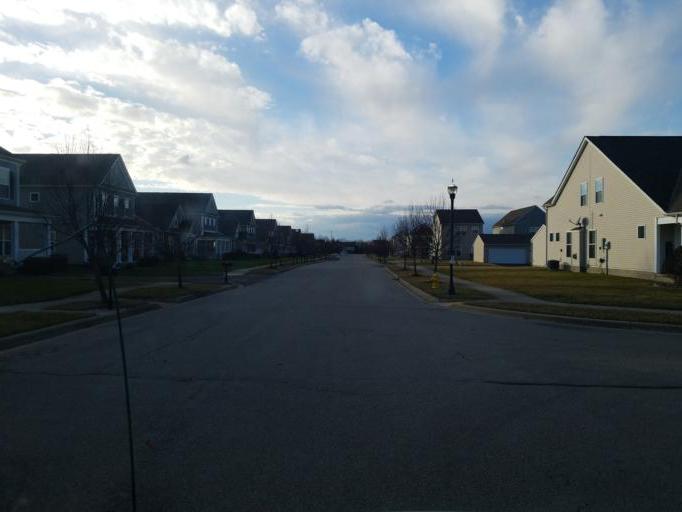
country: US
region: Ohio
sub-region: Delaware County
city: Delaware
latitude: 40.3196
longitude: -83.1055
